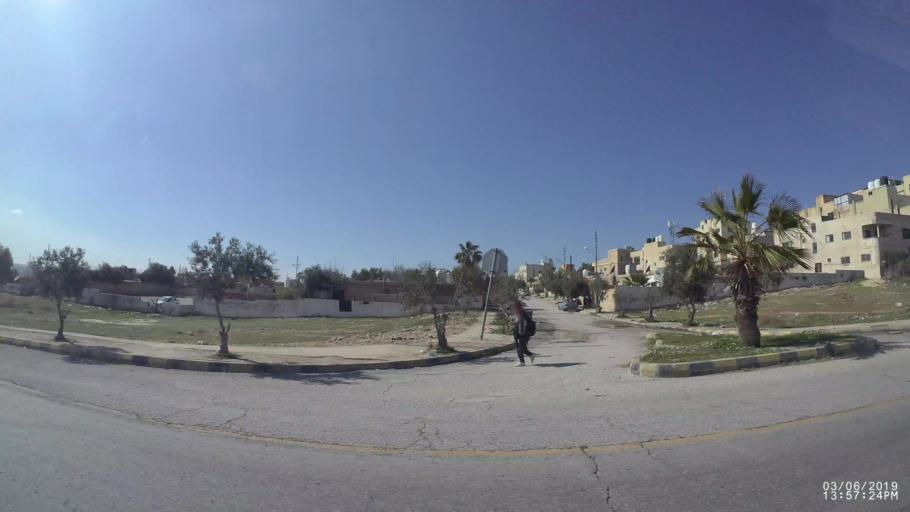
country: JO
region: Zarqa
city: Zarqa
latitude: 32.0328
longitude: 36.0997
